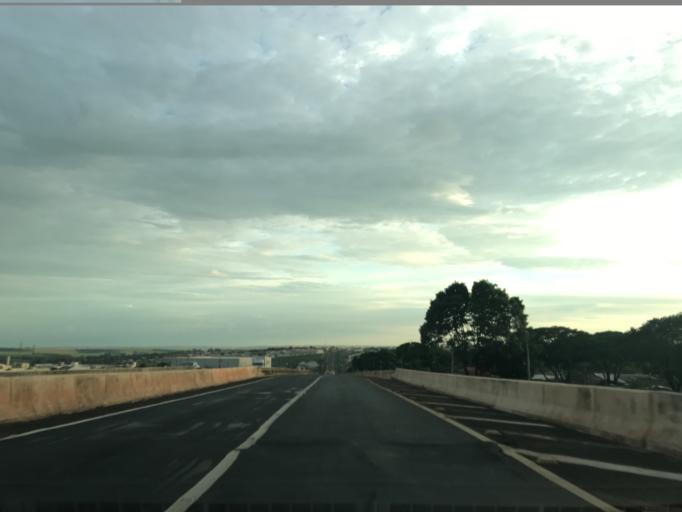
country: BR
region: Parana
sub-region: Maringa
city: Maringa
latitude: -23.3946
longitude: -51.9733
